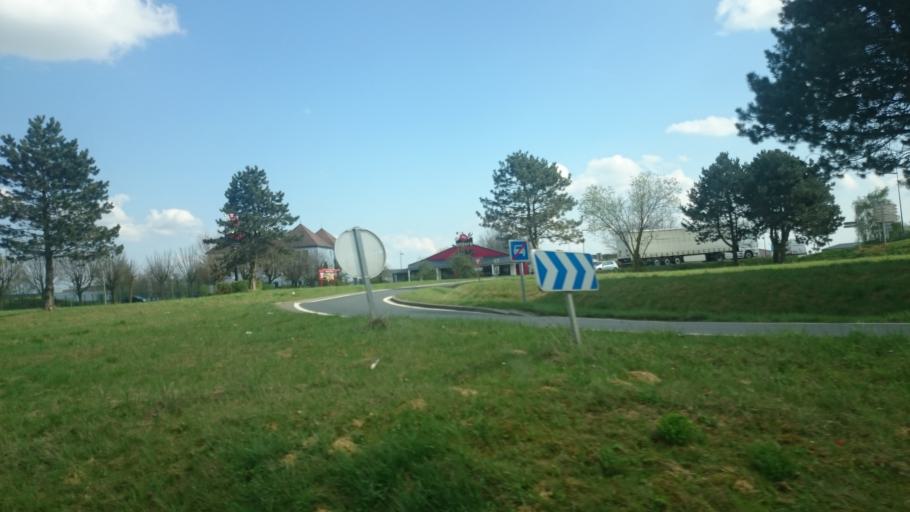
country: FR
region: Picardie
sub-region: Departement de l'Aisne
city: Gauchy
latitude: 49.8193
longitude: 3.2942
